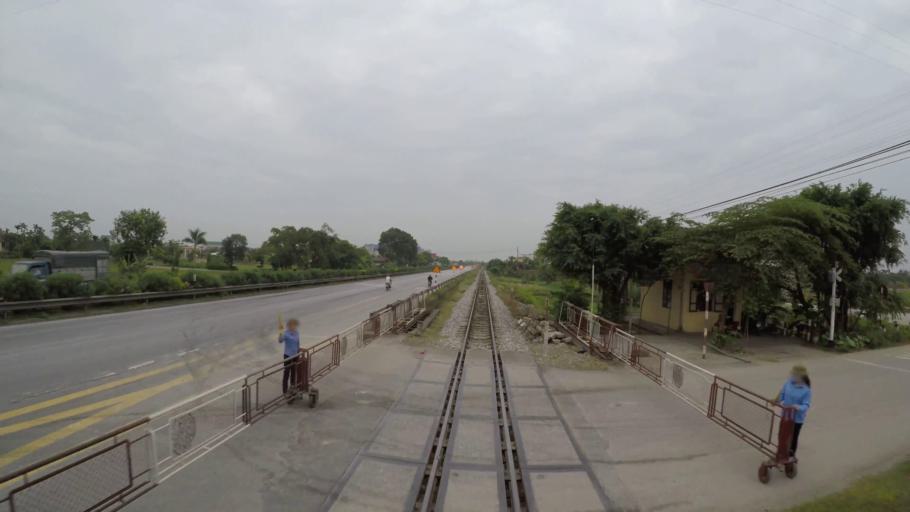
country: VN
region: Hai Duong
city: Thanh Ha
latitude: 20.9765
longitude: 106.4318
